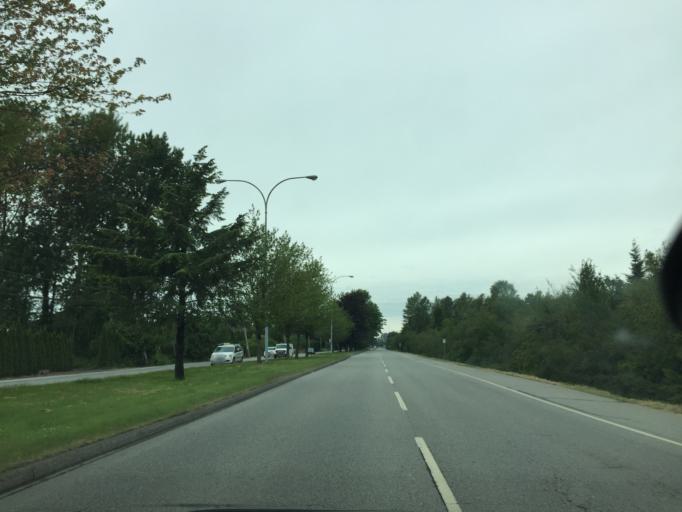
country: CA
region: British Columbia
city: Richmond
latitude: 49.1702
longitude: -123.1069
